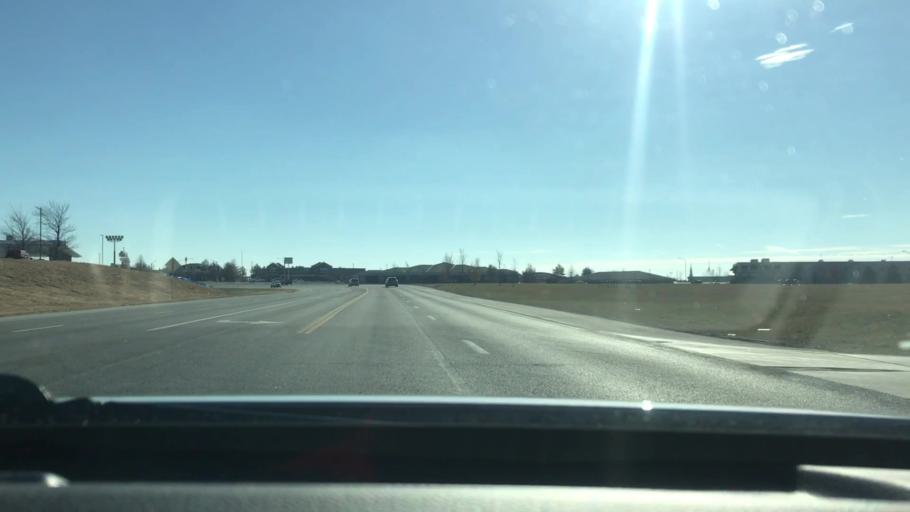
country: US
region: Missouri
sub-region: Platte County
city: Platte City
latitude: 39.3567
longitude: -94.7692
